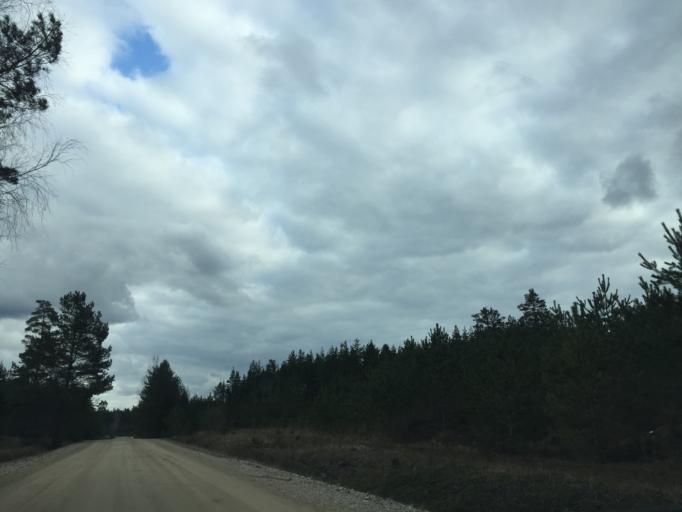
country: LV
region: Ogre
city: Jumprava
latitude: 56.5903
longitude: 24.9903
